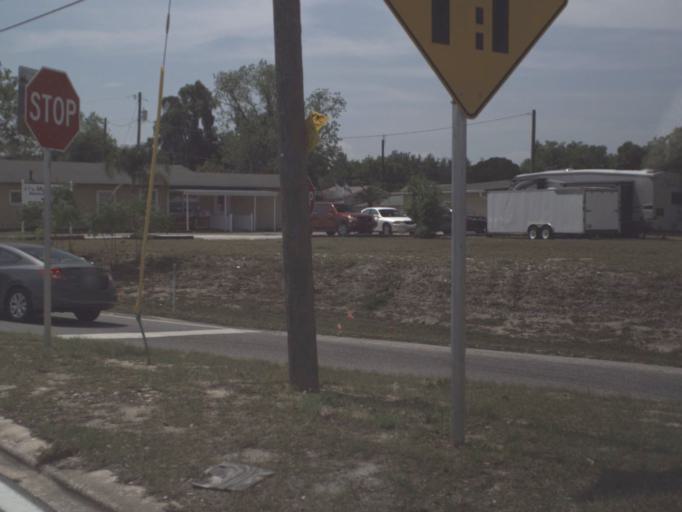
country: US
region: Florida
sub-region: Lake County
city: Eustis
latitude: 28.8217
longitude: -81.6856
